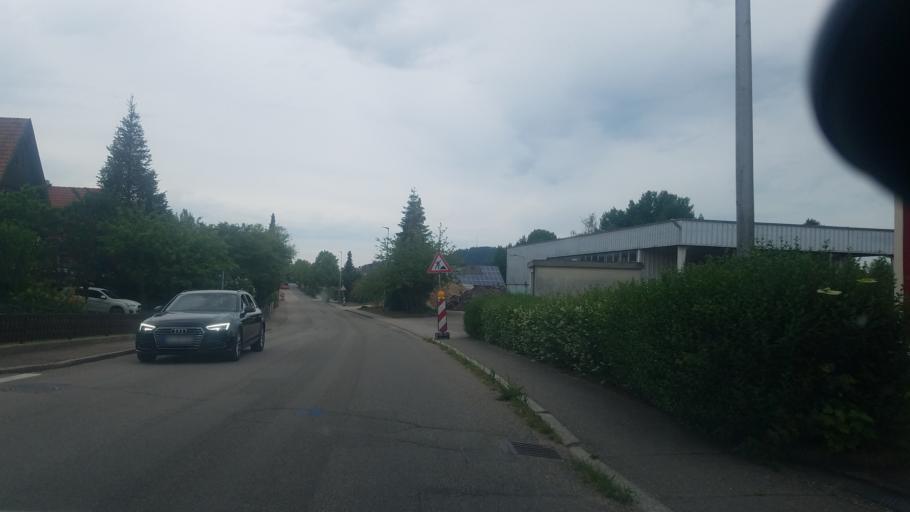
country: DE
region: Baden-Wuerttemberg
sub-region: Freiburg Region
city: Kappelrodeck
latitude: 48.5902
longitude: 8.1023
